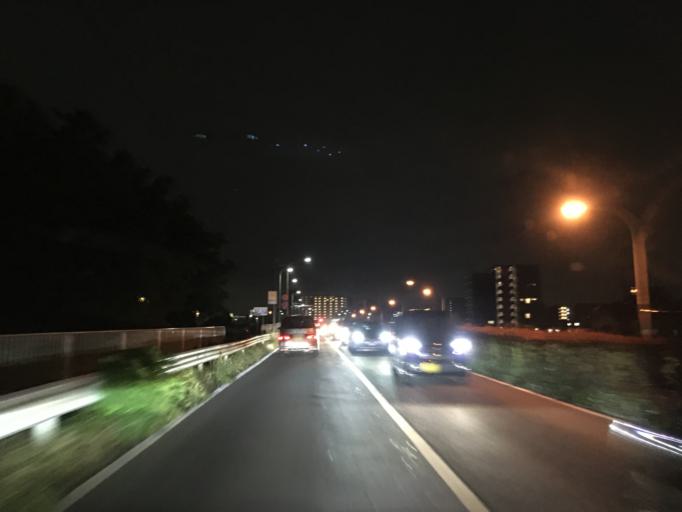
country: JP
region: Saitama
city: Sayama
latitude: 35.8610
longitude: 139.4025
